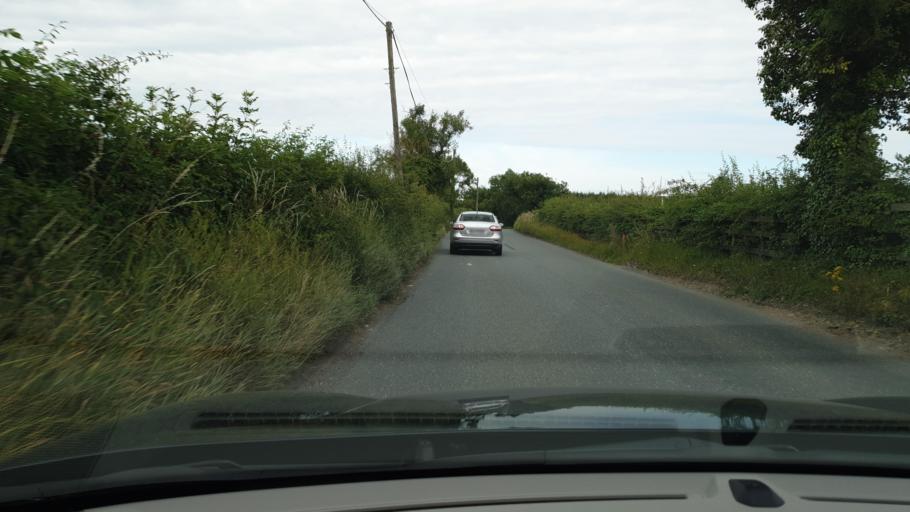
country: IE
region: Leinster
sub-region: An Mhi
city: Ashbourne
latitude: 53.5265
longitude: -6.4095
